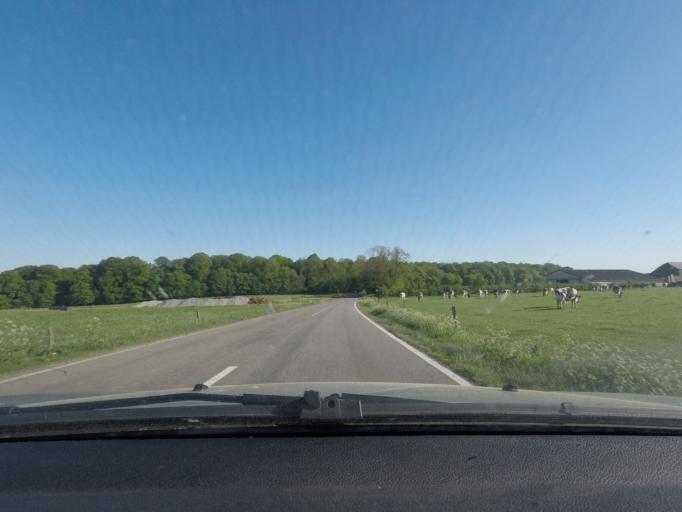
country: BE
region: Wallonia
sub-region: Province de Namur
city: Rochefort
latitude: 50.2147
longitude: 5.1479
